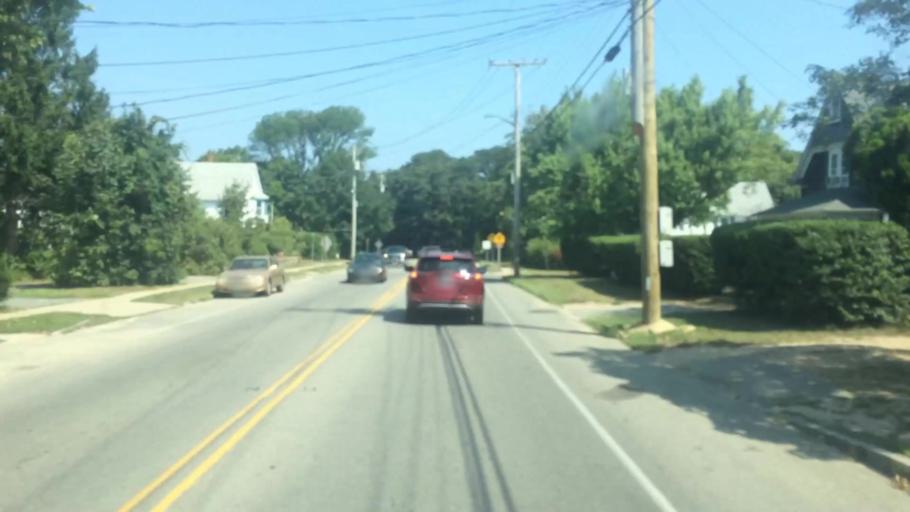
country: US
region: Massachusetts
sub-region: Dukes County
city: Vineyard Haven
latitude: 41.4496
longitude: -70.6067
